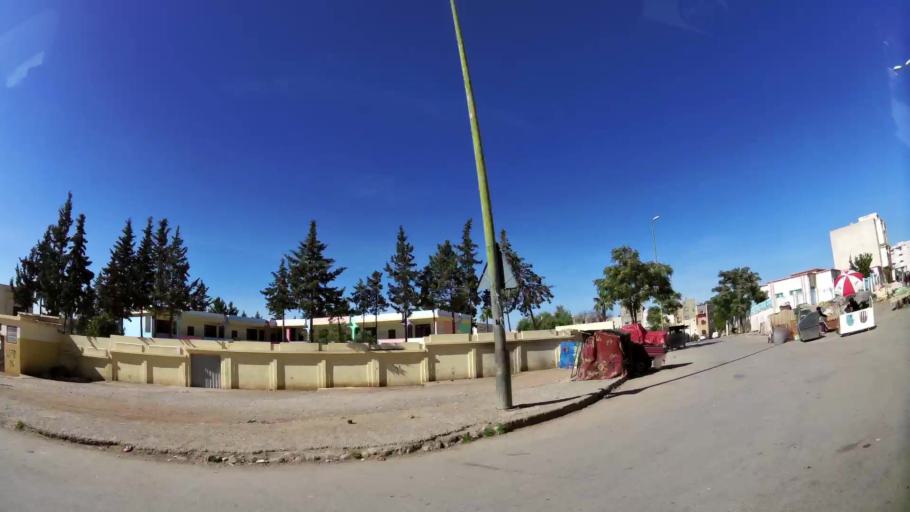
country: MA
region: Fes-Boulemane
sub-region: Fes
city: Fes
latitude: 34.0183
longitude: -4.9673
